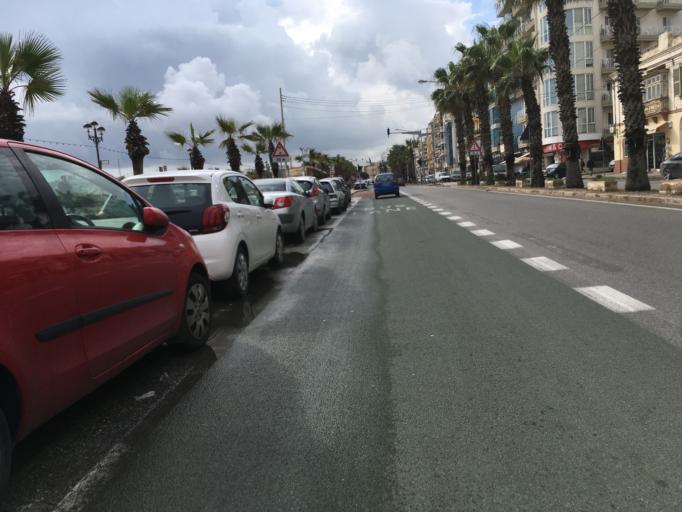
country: MT
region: Tas-Sliema
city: Sliema
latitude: 35.9065
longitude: 14.4978
